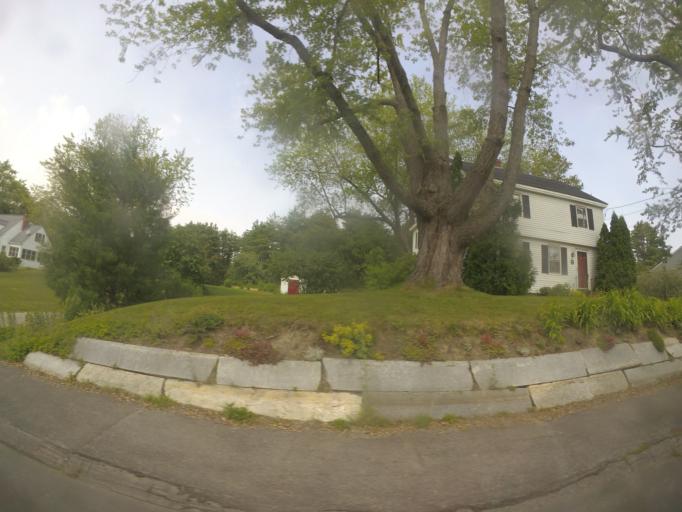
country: US
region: Maine
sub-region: Cumberland County
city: Falmouth
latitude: 43.7204
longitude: -70.2296
